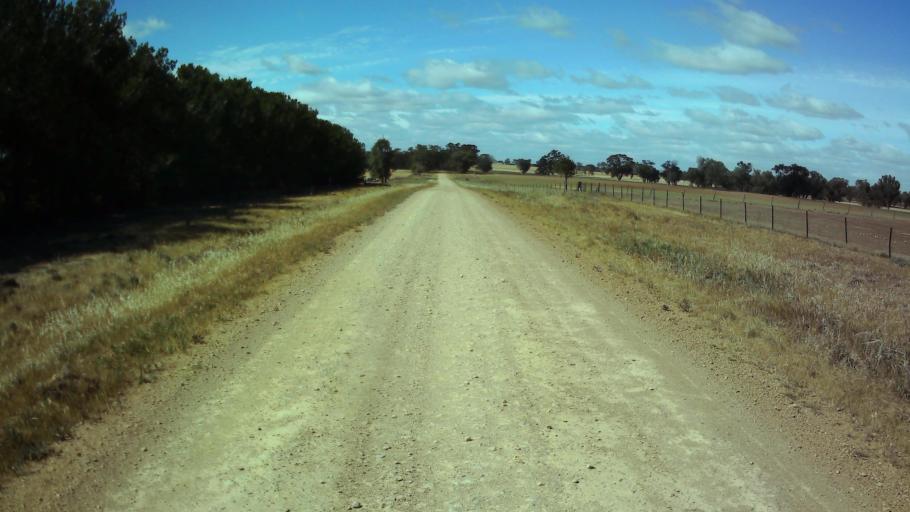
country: AU
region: New South Wales
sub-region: Weddin
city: Grenfell
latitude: -34.0593
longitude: 148.3123
